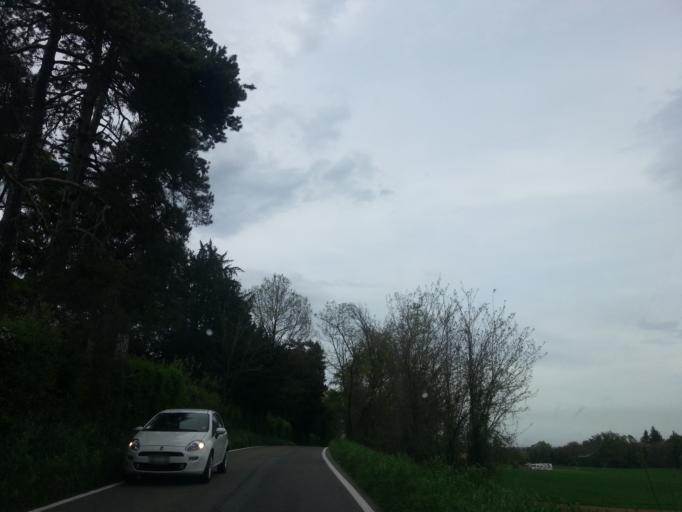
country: IT
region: Emilia-Romagna
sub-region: Provincia di Reggio Emilia
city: Albinea
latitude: 44.6368
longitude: 10.6017
